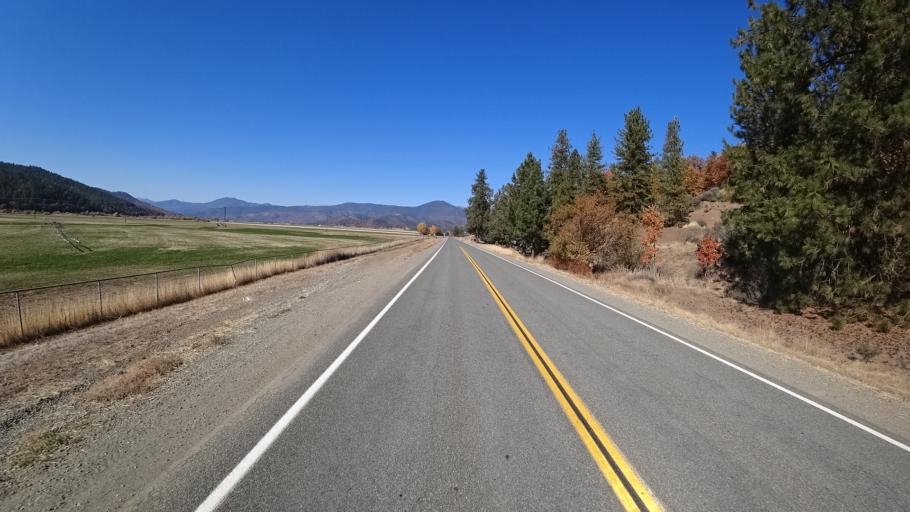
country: US
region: California
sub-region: Siskiyou County
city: Yreka
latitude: 41.6088
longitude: -122.8534
